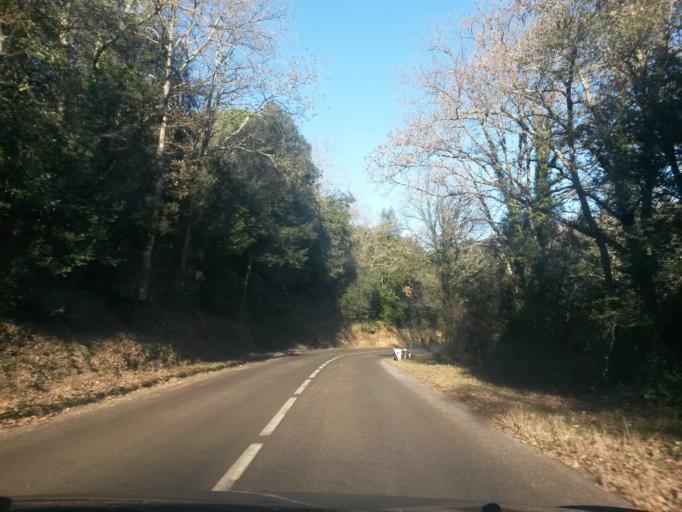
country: ES
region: Catalonia
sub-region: Provincia de Girona
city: la Cellera de Ter
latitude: 42.0213
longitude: 2.6689
